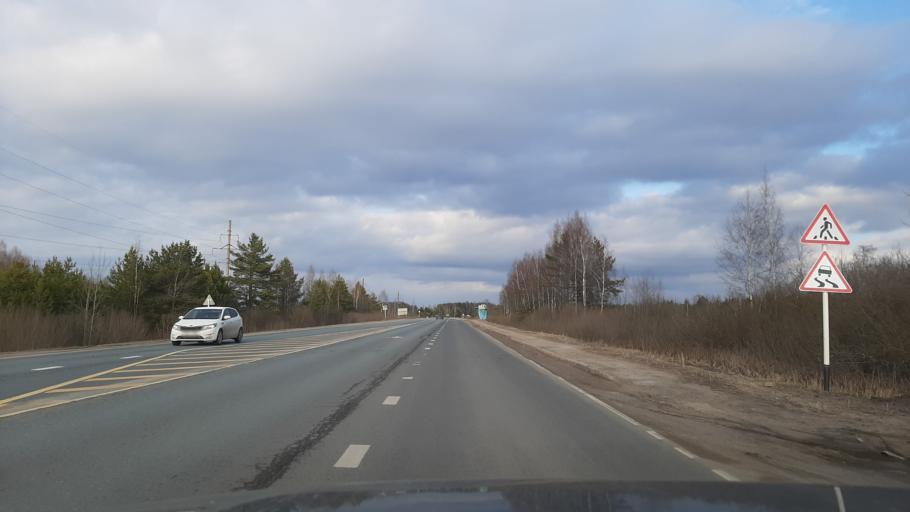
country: RU
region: Ivanovo
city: Novo-Talitsy
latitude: 56.9424
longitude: 40.7112
